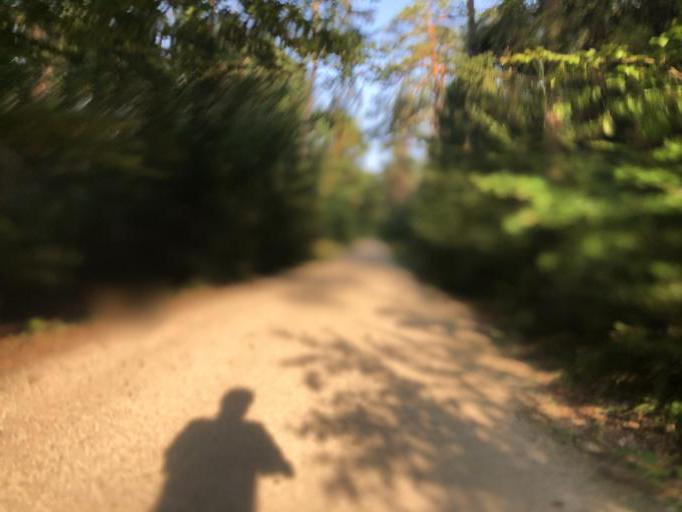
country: DE
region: Bavaria
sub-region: Regierungsbezirk Mittelfranken
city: Uttenreuth
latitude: 49.5677
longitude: 11.0818
